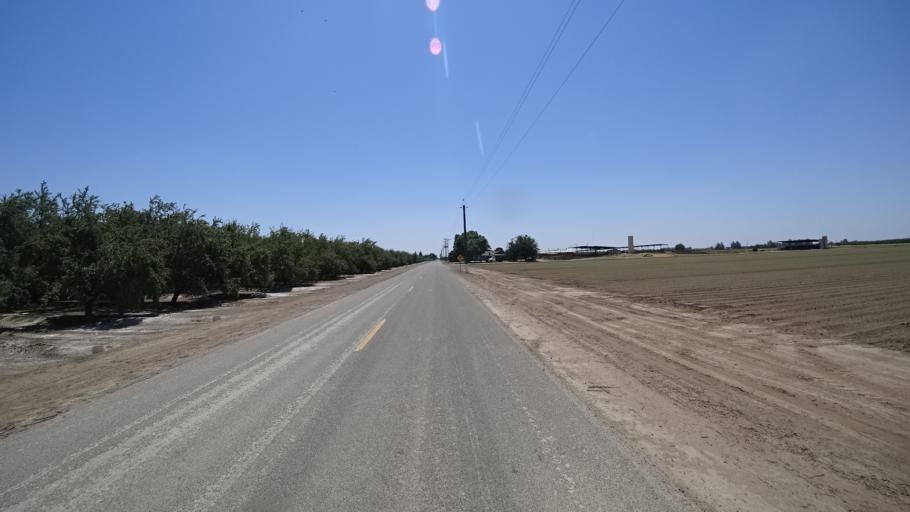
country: US
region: California
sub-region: Kings County
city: Armona
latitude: 36.3221
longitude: -119.7270
